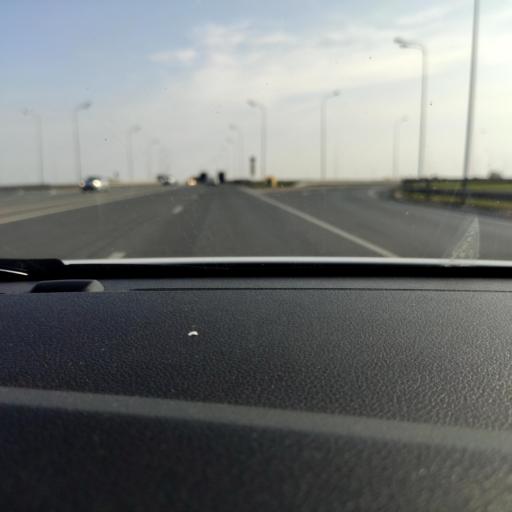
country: RU
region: Tatarstan
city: Vysokaya Gora
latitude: 55.8006
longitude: 49.3357
